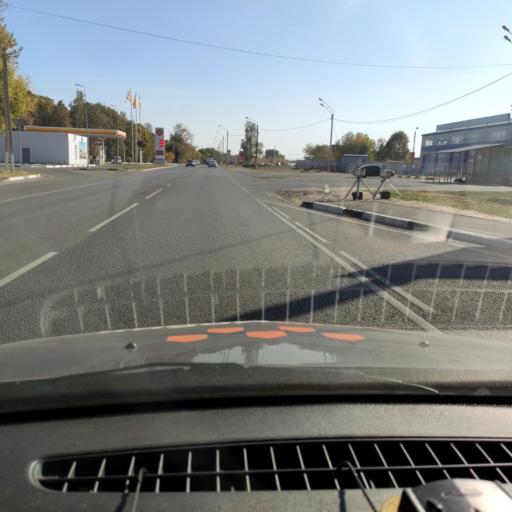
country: RU
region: Voronezj
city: Voronezh
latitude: 51.6181
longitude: 39.1772
